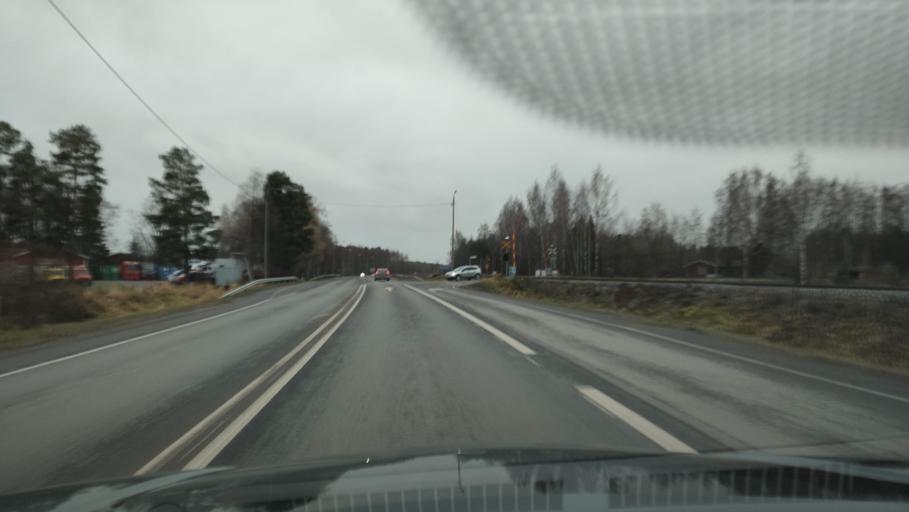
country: FI
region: Southern Ostrobothnia
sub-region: Seinaejoki
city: Ilmajoki
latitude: 62.7603
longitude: 22.6665
